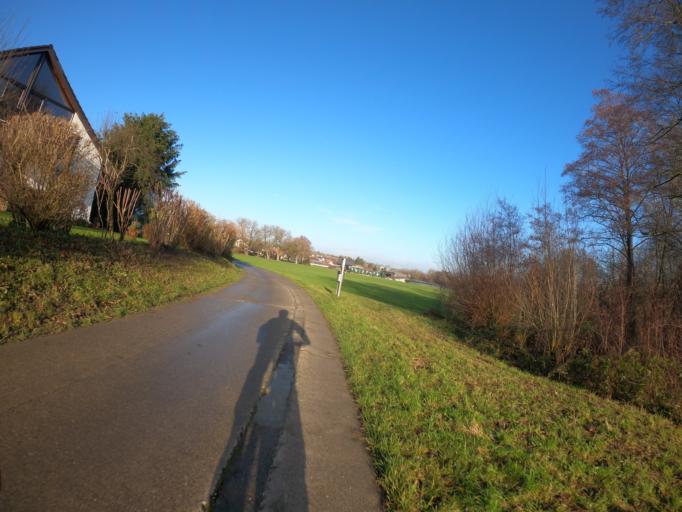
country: DE
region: Baden-Wuerttemberg
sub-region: Regierungsbezirk Stuttgart
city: Hattenhofen
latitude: 48.6634
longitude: 9.5786
